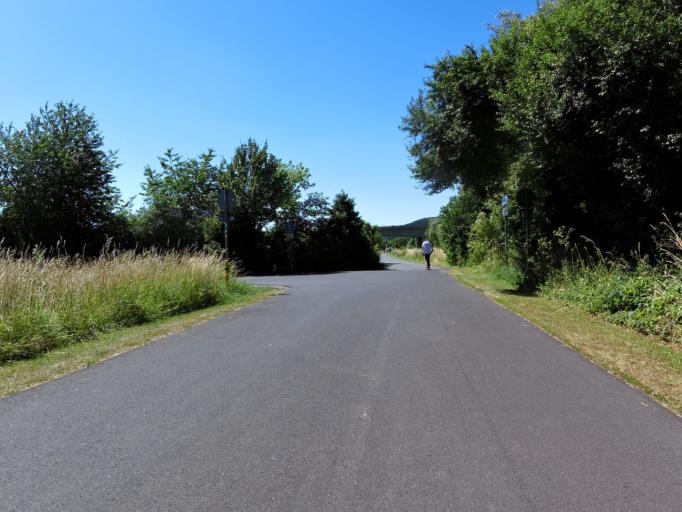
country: DE
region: Bavaria
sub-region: Regierungsbezirk Unterfranken
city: Randersacker
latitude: 49.7419
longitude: 9.9877
